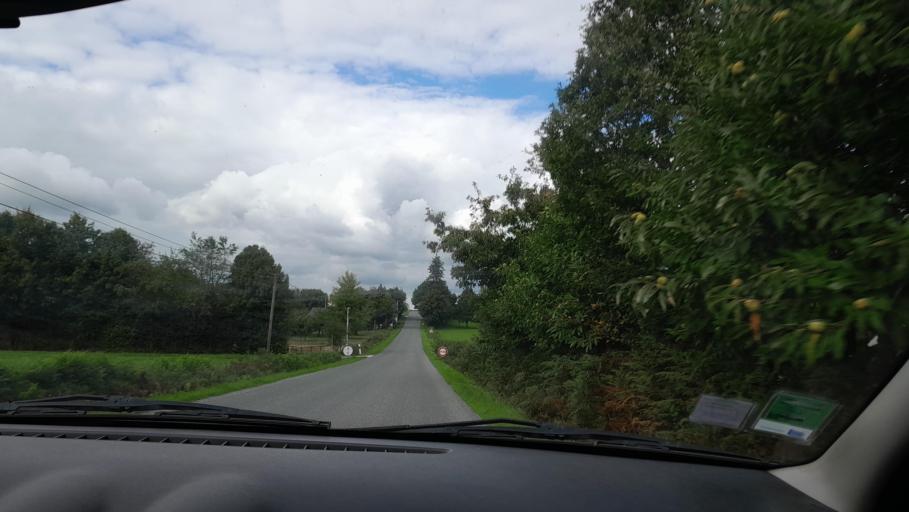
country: FR
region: Brittany
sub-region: Departement d'Ille-et-Vilaine
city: Le Pertre
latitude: 47.9789
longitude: -1.0414
